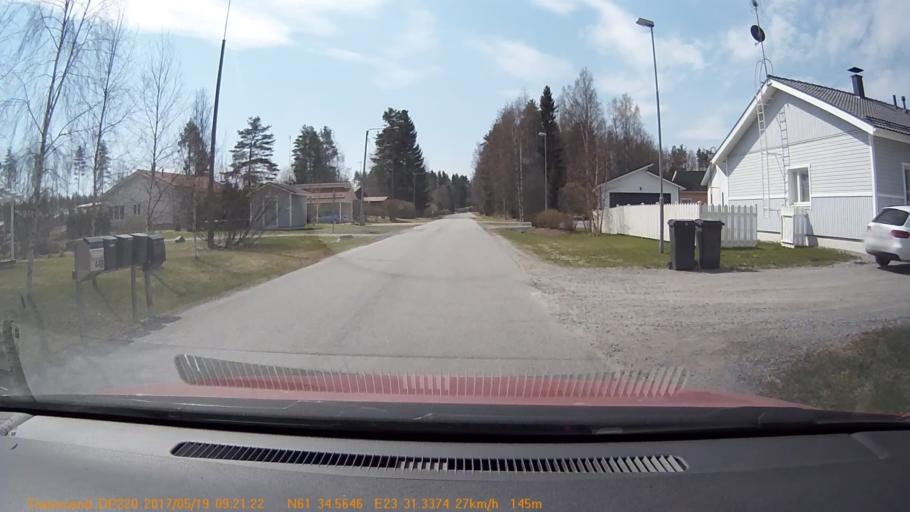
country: FI
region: Pirkanmaa
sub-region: Tampere
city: Yloejaervi
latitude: 61.5761
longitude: 23.5223
